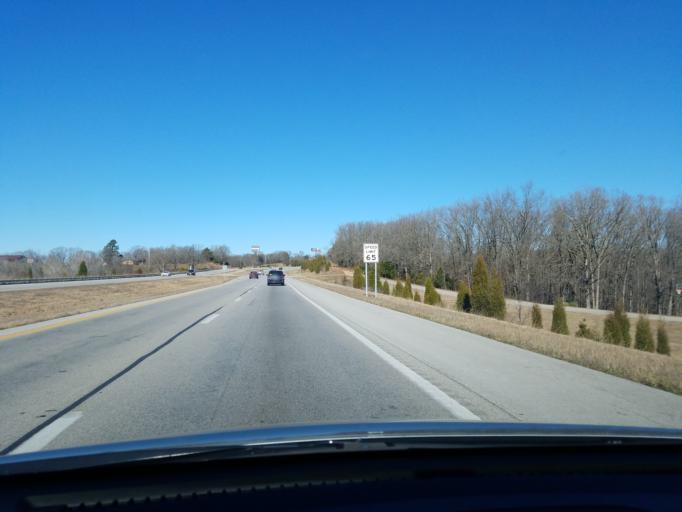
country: US
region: Missouri
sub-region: Taney County
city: Merriam Woods
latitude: 36.7939
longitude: -93.2255
